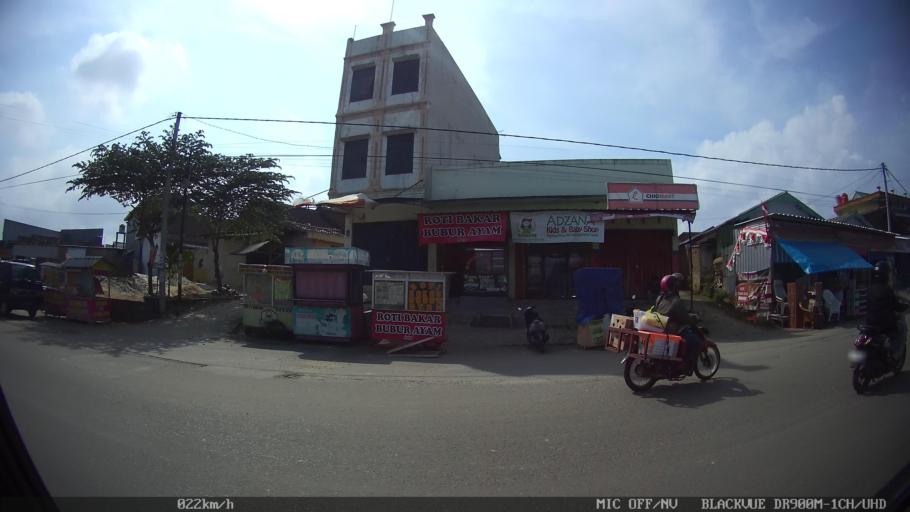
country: ID
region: Lampung
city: Kedaton
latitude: -5.3595
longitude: 105.2582
